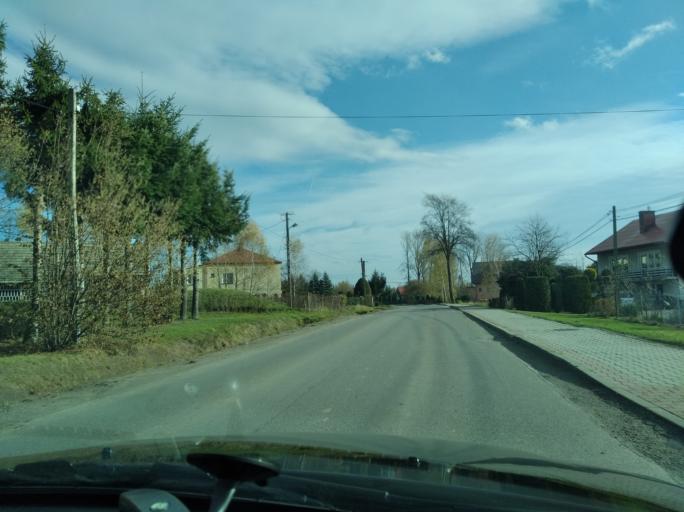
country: PL
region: Subcarpathian Voivodeship
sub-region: Powiat ropczycko-sedziszowski
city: Ostrow
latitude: 50.0985
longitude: 21.6243
